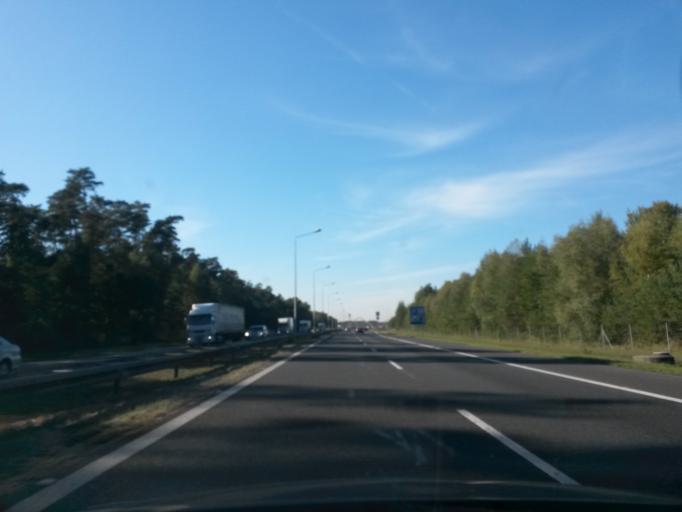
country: PL
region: Opole Voivodeship
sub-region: Powiat opolski
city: Niemodlin
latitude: 50.6727
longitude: 17.6635
